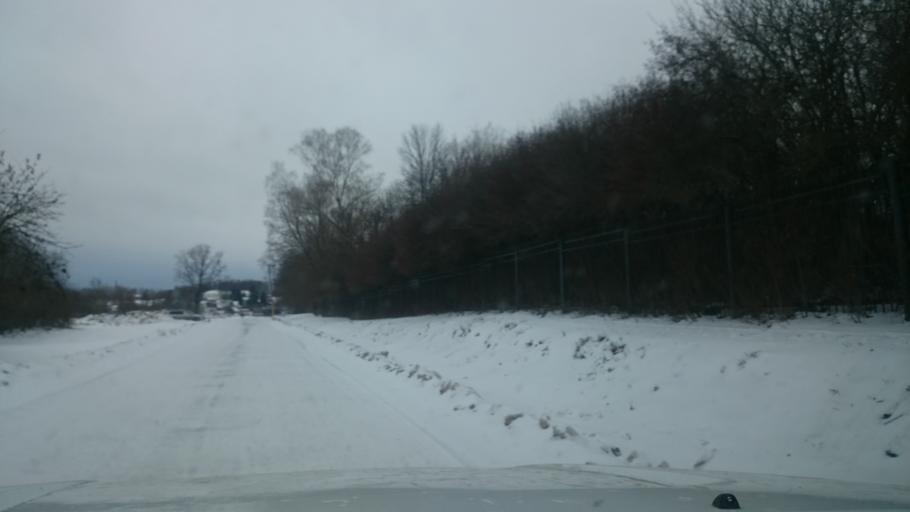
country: RU
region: Tula
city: Pervomayskiy
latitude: 54.0766
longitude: 37.5352
